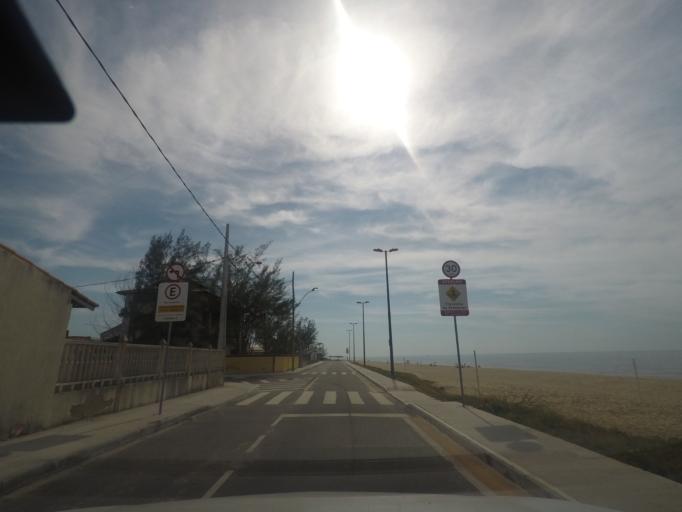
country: BR
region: Rio de Janeiro
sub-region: Marica
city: Marica
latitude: -22.9615
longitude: -42.8240
